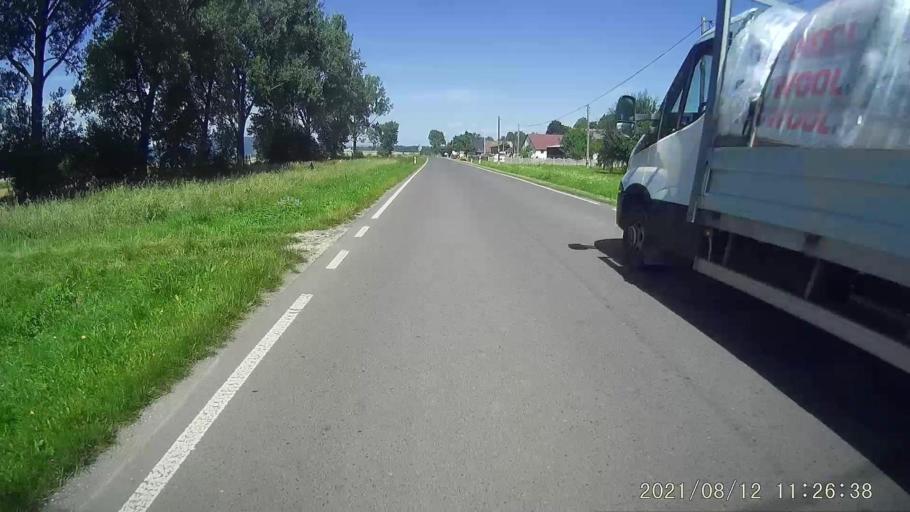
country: PL
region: Lower Silesian Voivodeship
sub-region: Powiat klodzki
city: Bystrzyca Klodzka
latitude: 50.2751
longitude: 16.6871
